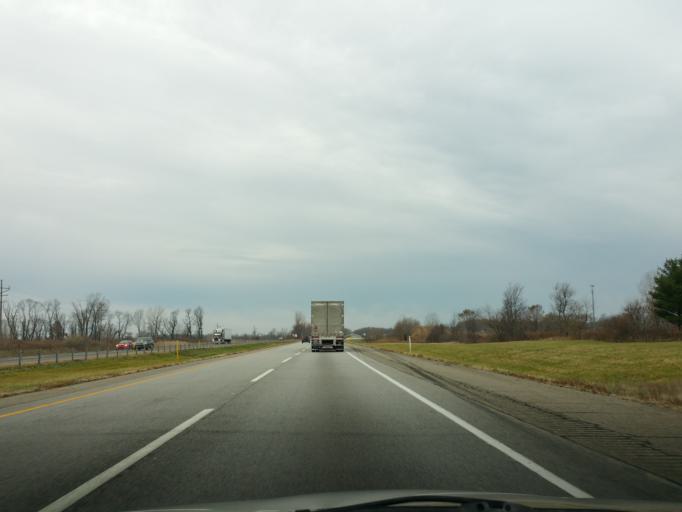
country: US
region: Indiana
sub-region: Porter County
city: South Haven
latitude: 41.5721
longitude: -87.1436
